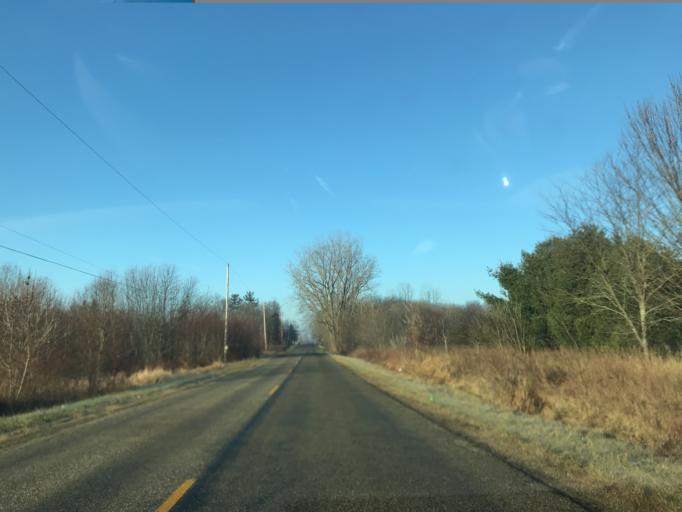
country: US
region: Michigan
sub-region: Eaton County
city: Dimondale
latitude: 42.6620
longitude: -84.6163
